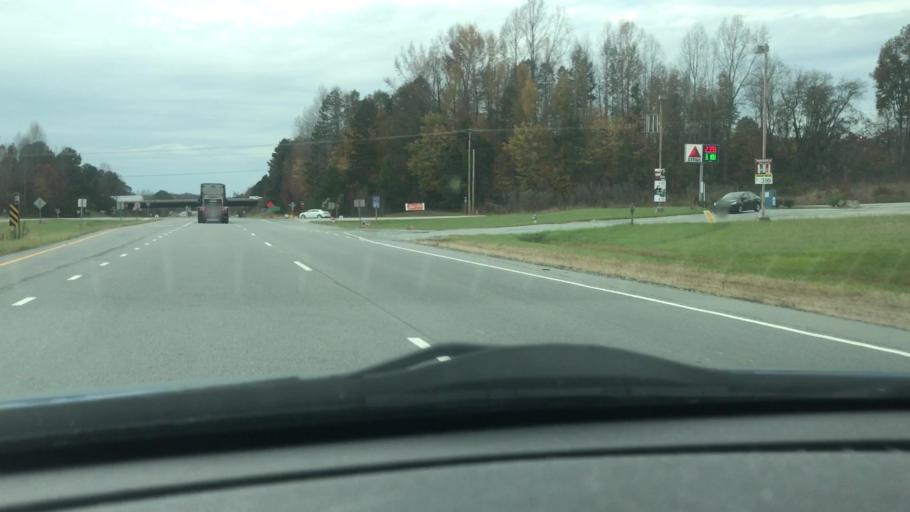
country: US
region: North Carolina
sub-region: Davidson County
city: Lexington
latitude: 35.8084
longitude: -80.1778
